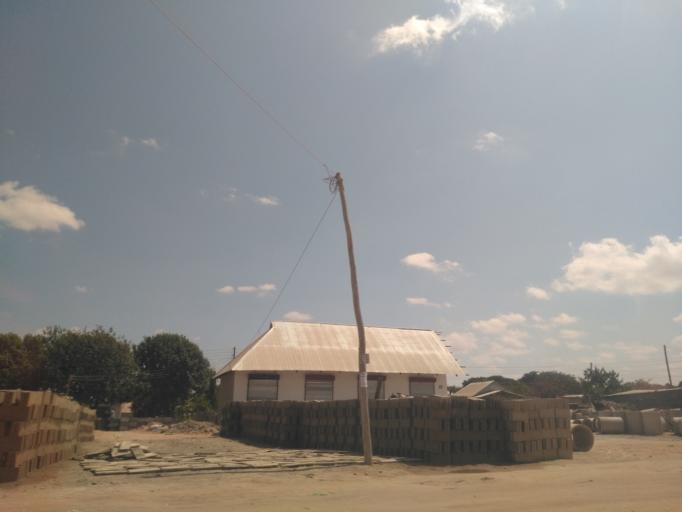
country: TZ
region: Dodoma
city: Dodoma
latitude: -6.1596
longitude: 35.7457
